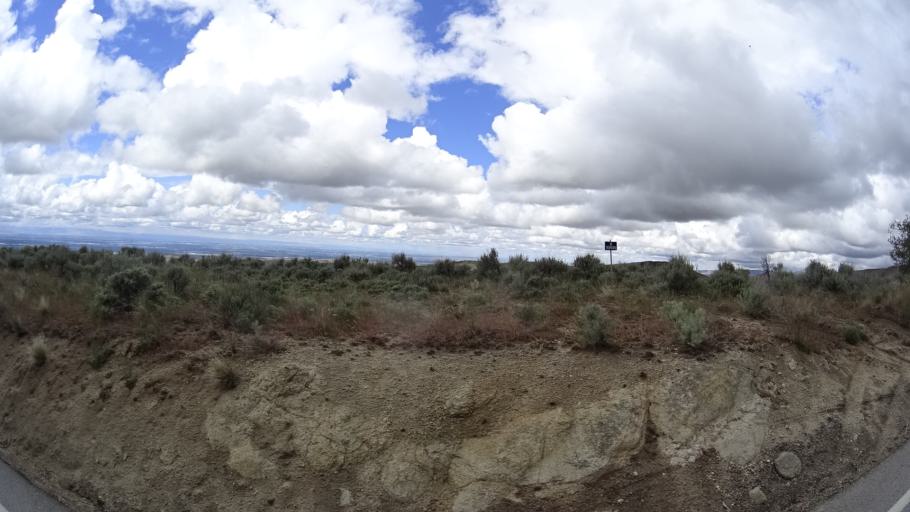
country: US
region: Idaho
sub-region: Ada County
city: Boise
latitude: 43.7074
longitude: -116.1654
